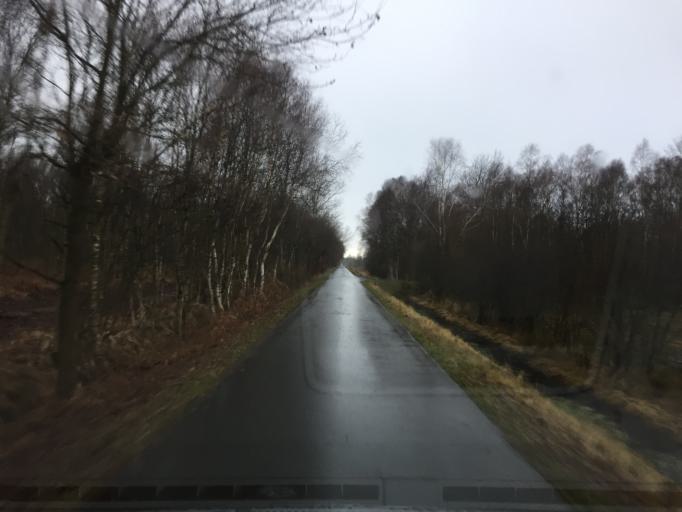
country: DE
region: Lower Saxony
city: Maasen
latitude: 52.6544
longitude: 8.8574
